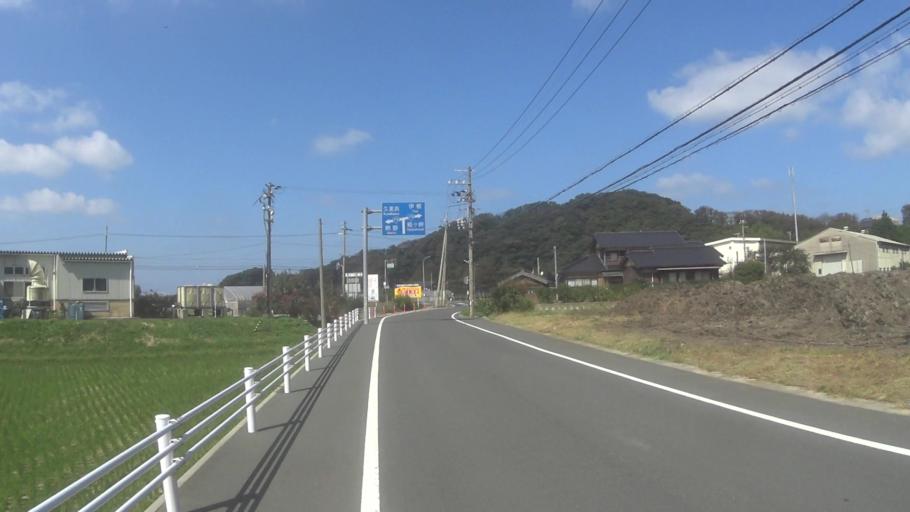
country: JP
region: Kyoto
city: Miyazu
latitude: 35.7395
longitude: 135.1099
